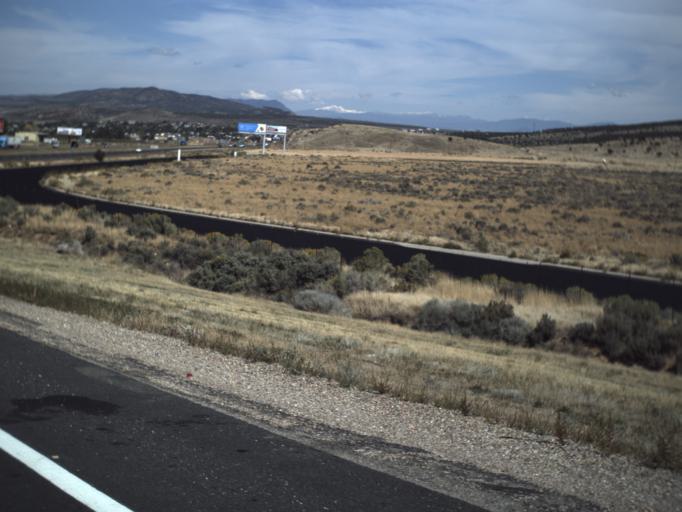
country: US
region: Utah
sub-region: Iron County
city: Enoch
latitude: 37.7287
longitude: -113.0506
